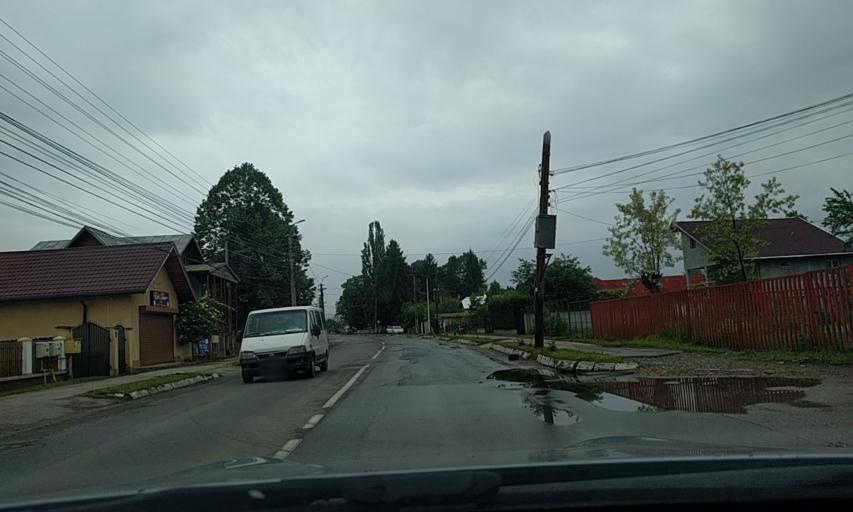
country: RO
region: Dambovita
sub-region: Oras Pucioasa
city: Glodeni
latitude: 45.0582
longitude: 25.4387
